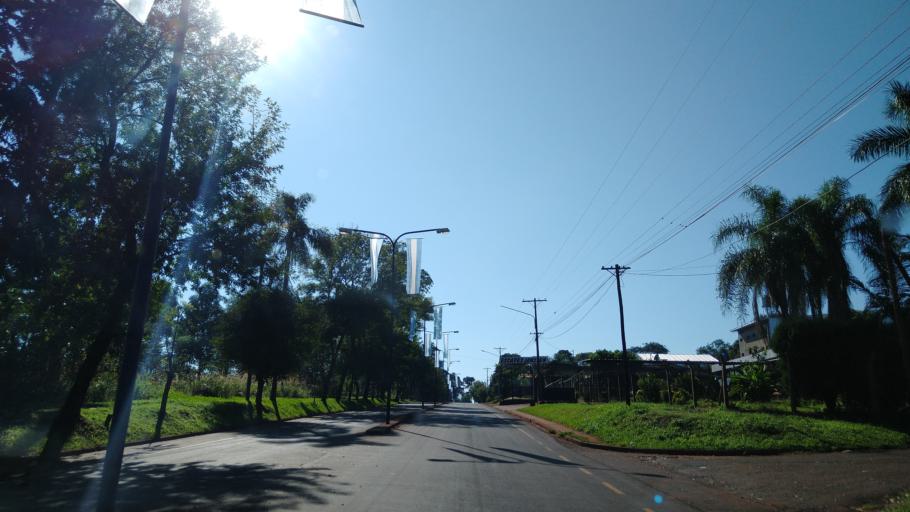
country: AR
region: Misiones
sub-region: Departamento de Montecarlo
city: Montecarlo
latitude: -26.5715
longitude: -54.7382
